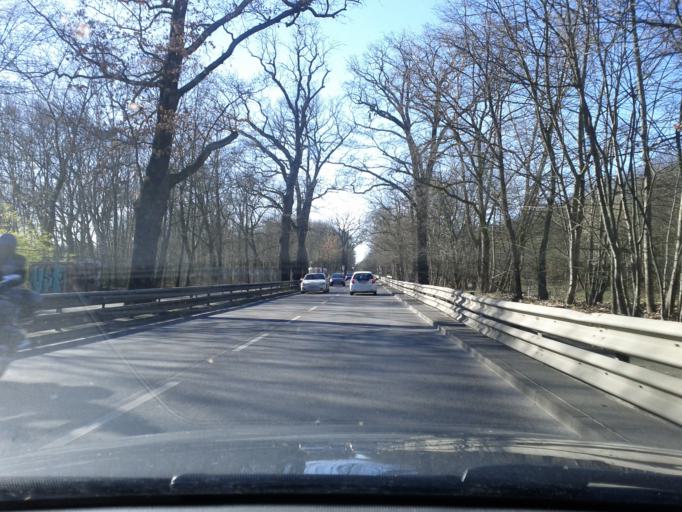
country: DE
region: Berlin
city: Rahnsdorf
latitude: 52.4467
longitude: 13.6729
